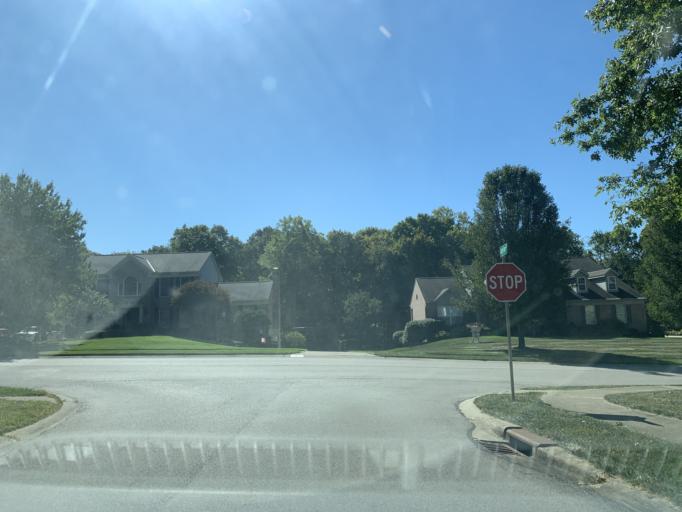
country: US
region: Kentucky
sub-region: Boone County
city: Francisville
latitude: 39.0989
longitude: -84.7290
